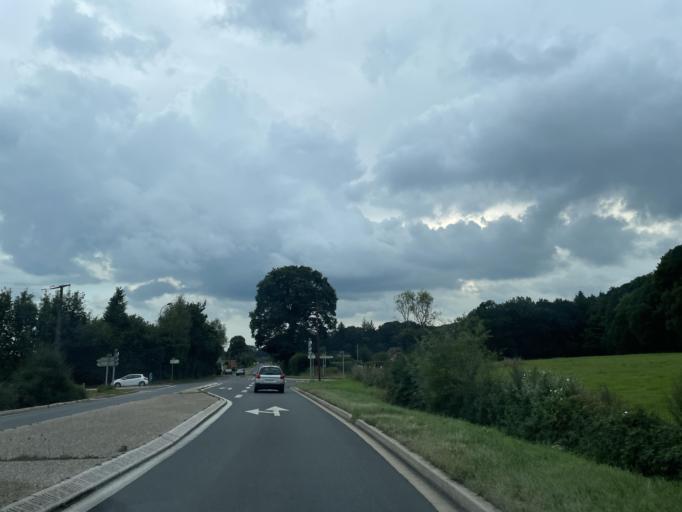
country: FR
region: Haute-Normandie
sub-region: Departement de la Seine-Maritime
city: Cayenne
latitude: 49.5833
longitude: 1.5972
